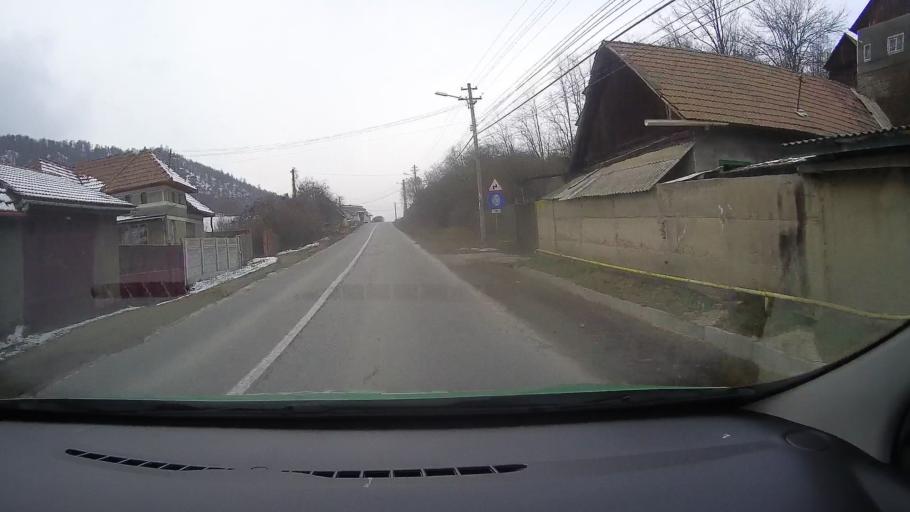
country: RO
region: Alba
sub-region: Oras Zlatna
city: Zlatna
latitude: 46.0922
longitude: 23.2576
